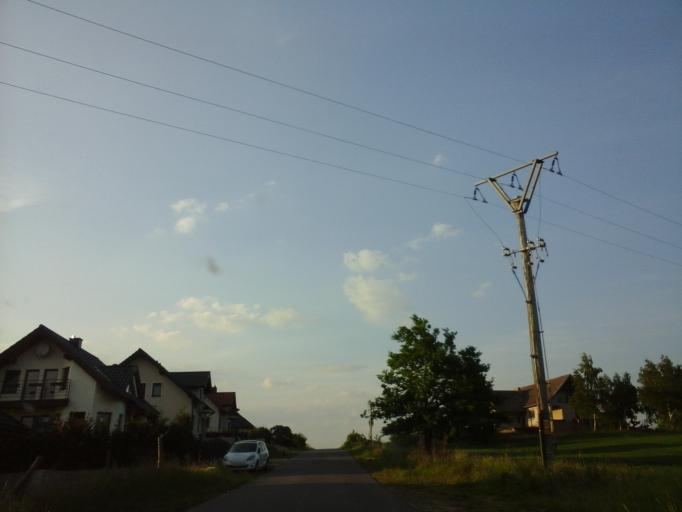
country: PL
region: West Pomeranian Voivodeship
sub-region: Powiat choszczenski
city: Choszczno
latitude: 53.1816
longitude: 15.4149
